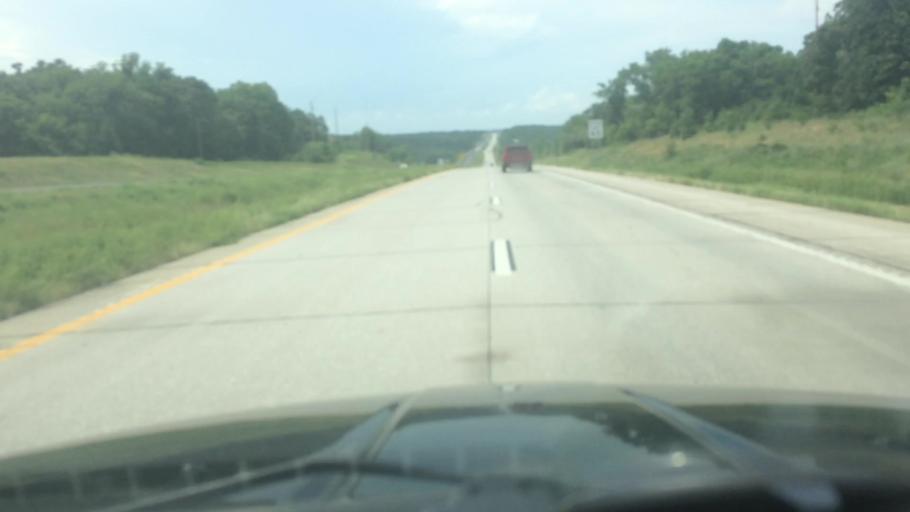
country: US
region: Missouri
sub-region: Saint Clair County
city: Osceola
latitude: 38.0474
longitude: -93.6852
